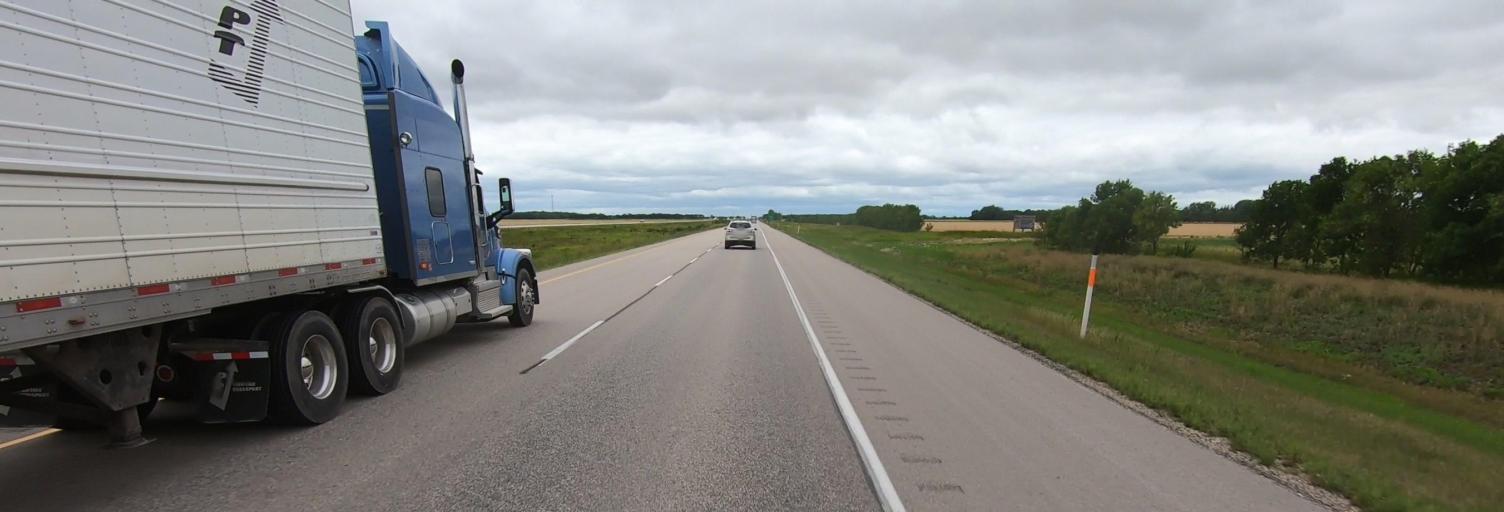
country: CA
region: Manitoba
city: Portage la Prairie
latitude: 49.9473
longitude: -97.9743
